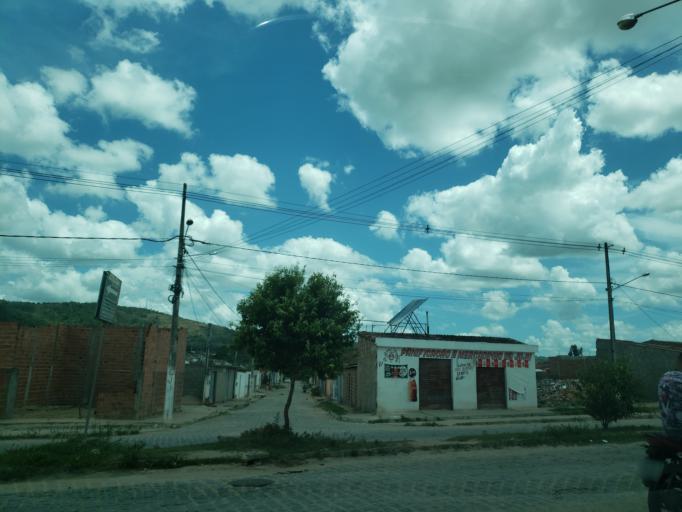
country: BR
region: Alagoas
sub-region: Uniao Dos Palmares
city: Uniao dos Palmares
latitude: -9.1503
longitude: -36.0088
